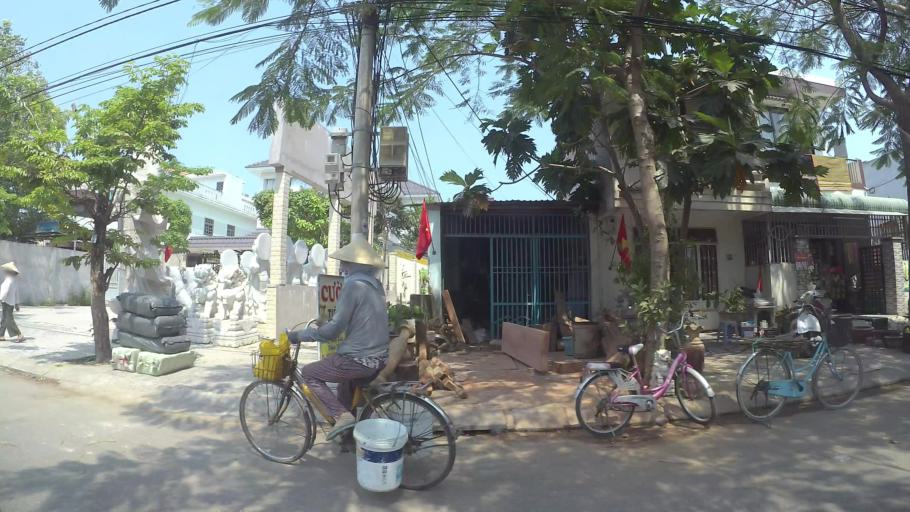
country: VN
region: Da Nang
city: Ngu Hanh Son
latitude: 15.9966
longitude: 108.2632
